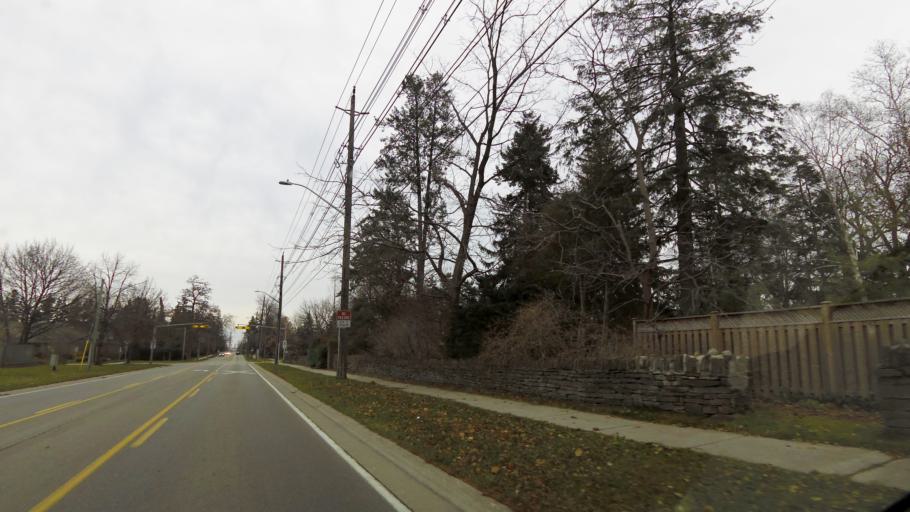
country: CA
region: Ontario
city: Oakville
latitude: 43.4787
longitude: -79.6326
